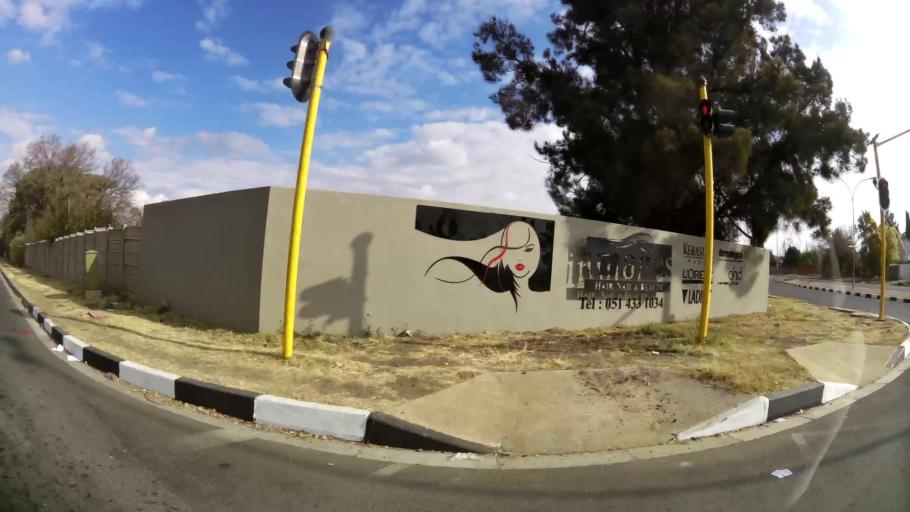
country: ZA
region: Orange Free State
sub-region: Mangaung Metropolitan Municipality
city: Bloemfontein
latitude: -29.0743
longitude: 26.2364
